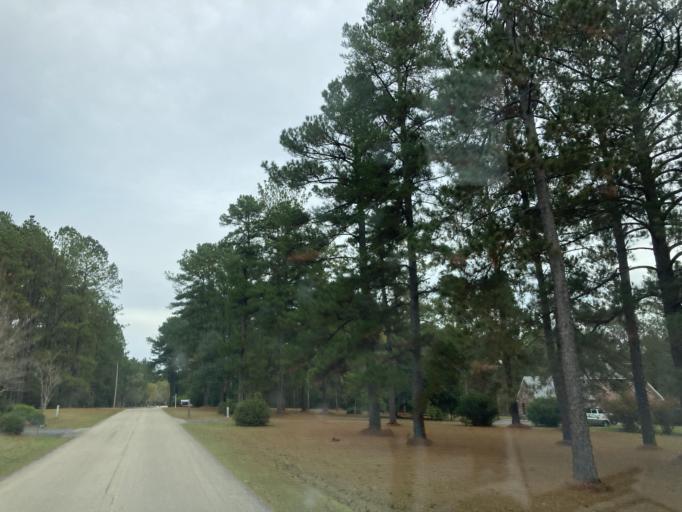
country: US
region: Mississippi
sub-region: Lamar County
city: Purvis
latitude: 31.1409
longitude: -89.4609
